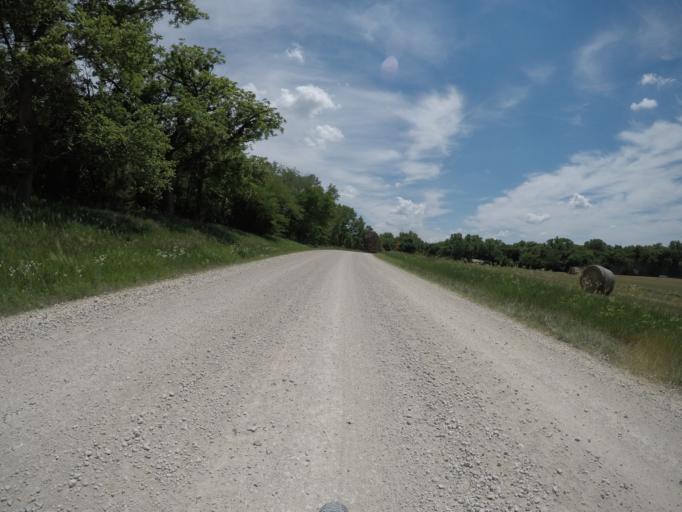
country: US
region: Kansas
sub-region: Wabaunsee County
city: Alma
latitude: 38.9231
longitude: -96.2227
